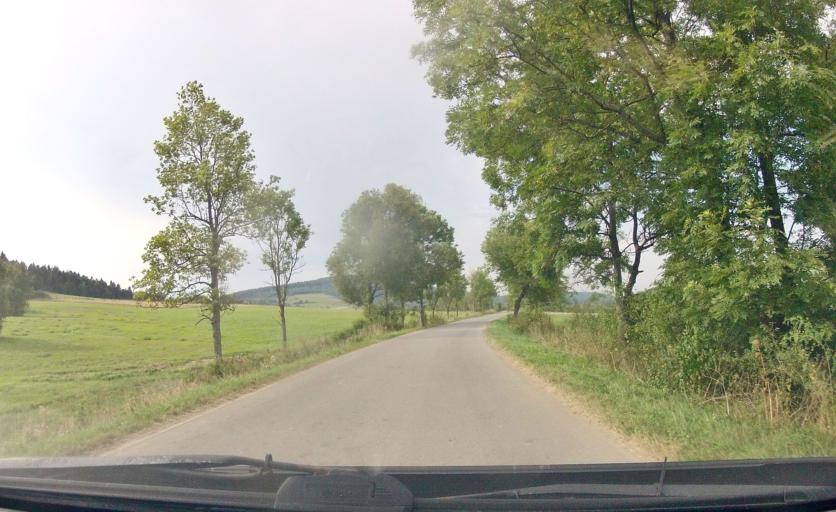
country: PL
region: Subcarpathian Voivodeship
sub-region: Powiat krosnienski
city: Dukla
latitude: 49.5130
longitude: 21.6253
